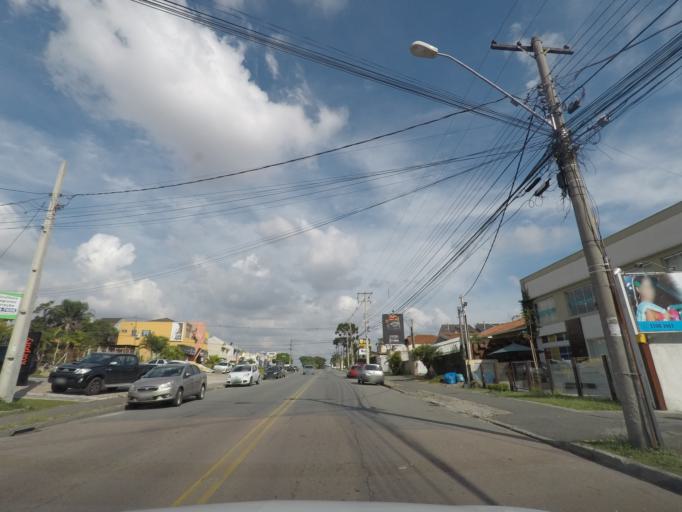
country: BR
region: Parana
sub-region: Pinhais
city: Pinhais
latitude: -25.4617
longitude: -49.2234
